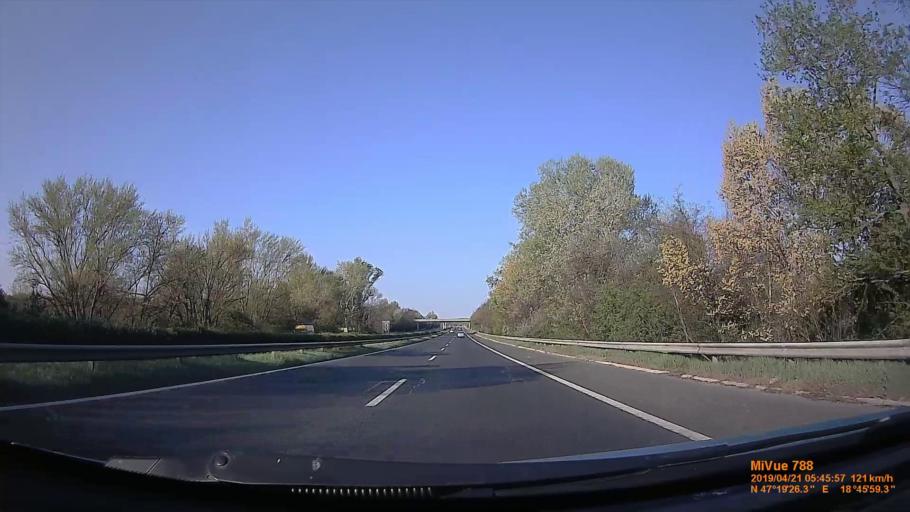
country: HU
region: Fejer
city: Martonvasar
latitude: 47.3238
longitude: 18.7661
